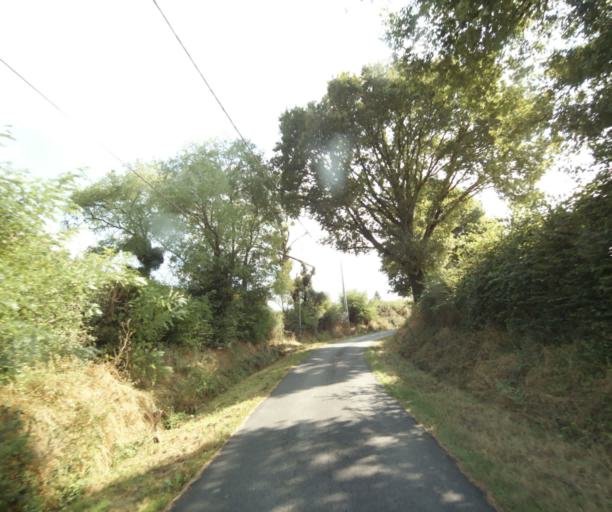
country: FR
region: Bourgogne
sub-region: Departement de Saone-et-Loire
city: Palinges
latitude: 46.5002
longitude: 4.2216
